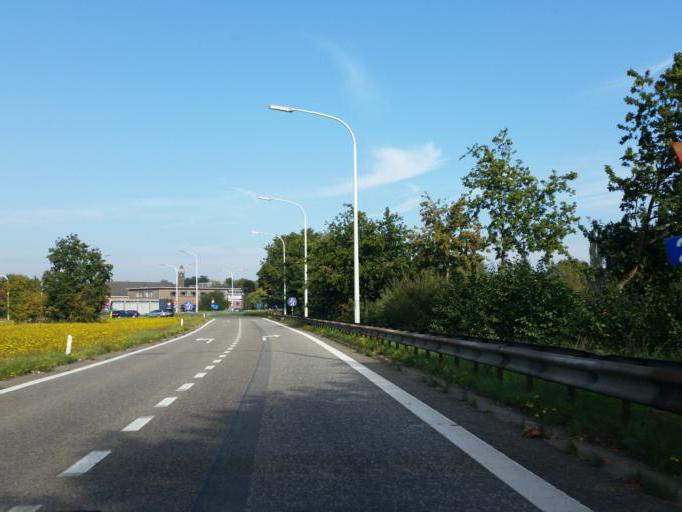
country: BE
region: Flanders
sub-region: Provincie Antwerpen
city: Kontich
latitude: 51.1270
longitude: 4.4342
